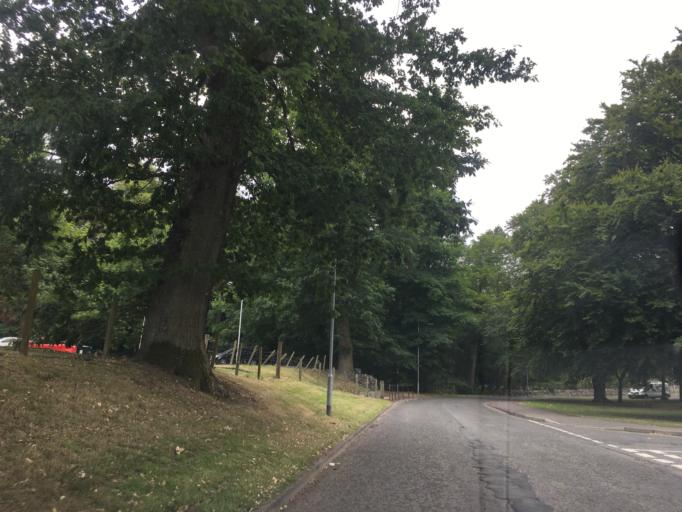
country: GB
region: Scotland
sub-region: The Scottish Borders
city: Peebles
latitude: 55.6432
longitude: -3.1834
